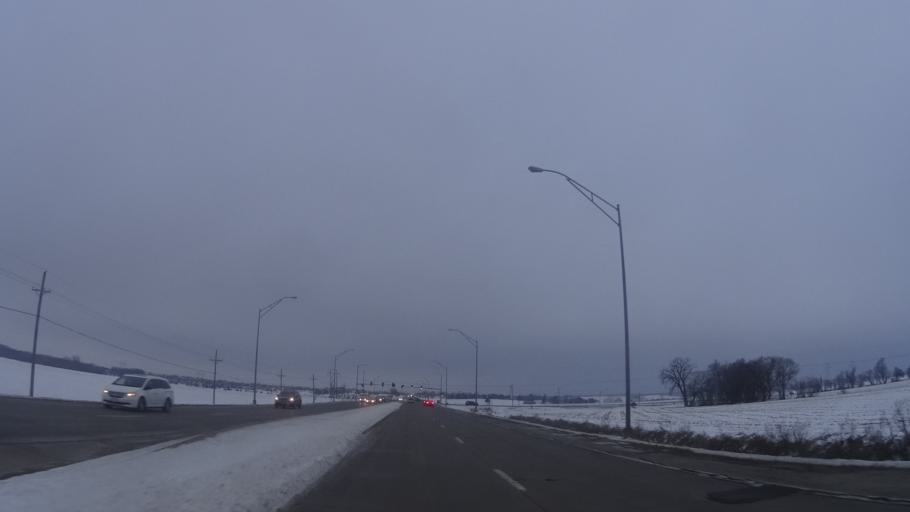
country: US
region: Nebraska
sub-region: Sarpy County
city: La Vista
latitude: 41.1618
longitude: -95.9816
